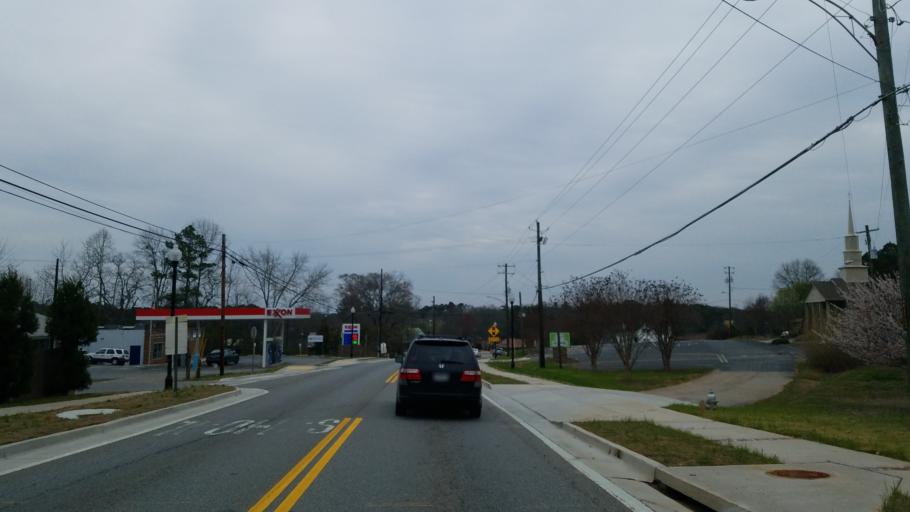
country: US
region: Georgia
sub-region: Cherokee County
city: Holly Springs
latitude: 34.1759
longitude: -84.5021
